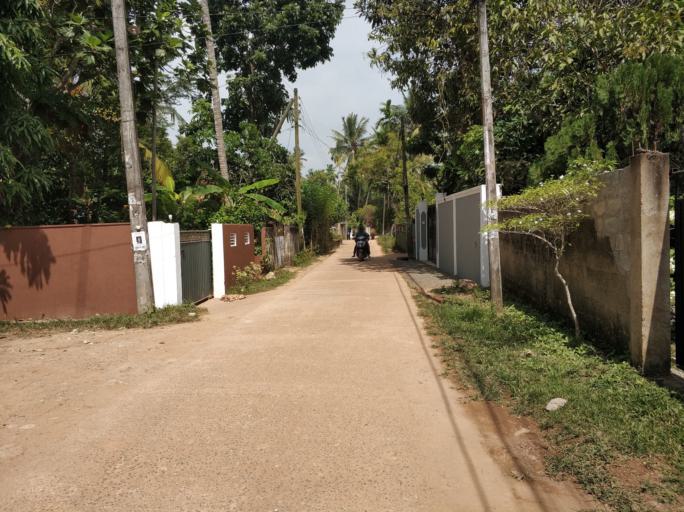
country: LK
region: Southern
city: Weligama
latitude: 5.9641
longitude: 80.4026
